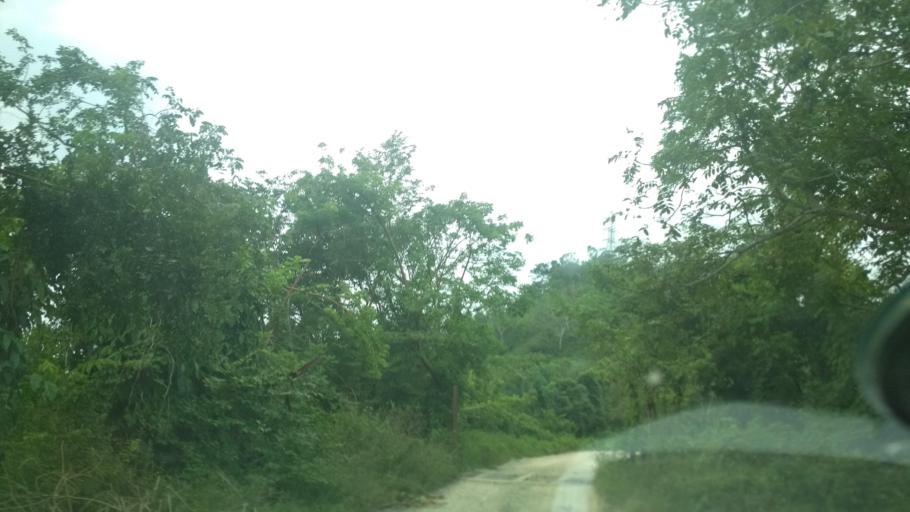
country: MX
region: Veracruz
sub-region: Poza Rica de Hidalgo
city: El Mollejon
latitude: 20.5270
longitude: -97.3903
